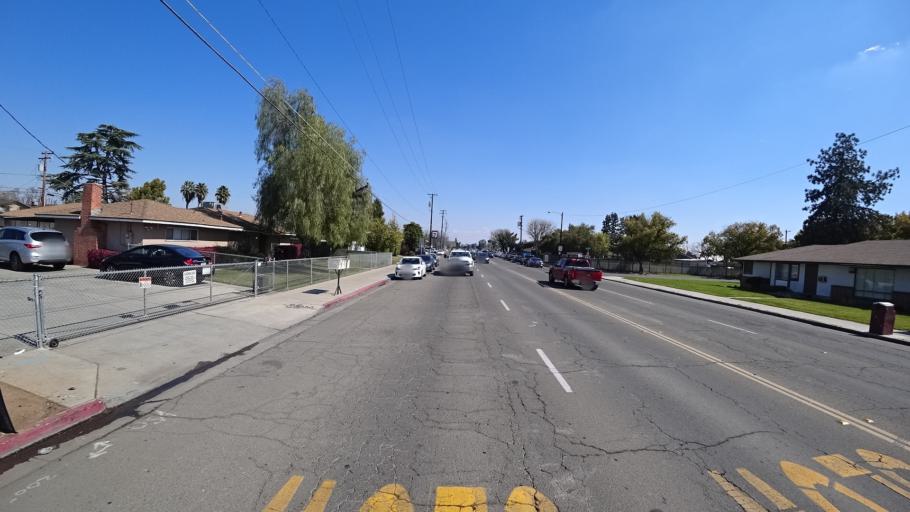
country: US
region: California
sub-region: Fresno County
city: Fresno
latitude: 36.7941
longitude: -119.7928
